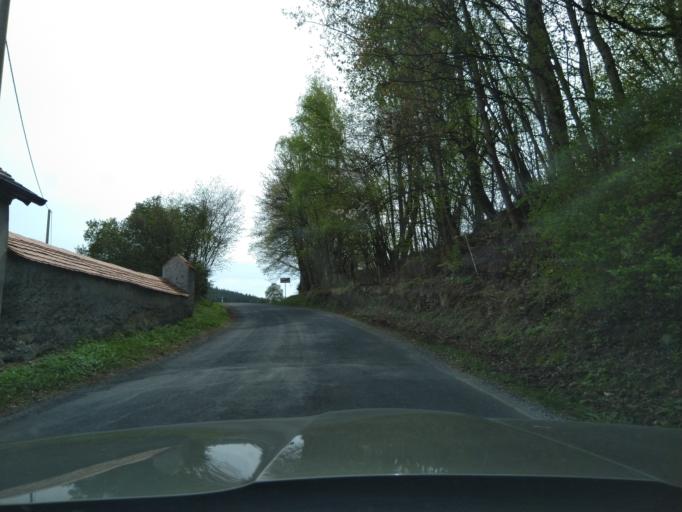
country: CZ
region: Jihocesky
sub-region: Okres Prachatice
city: Stachy
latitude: 49.1814
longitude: 13.6507
